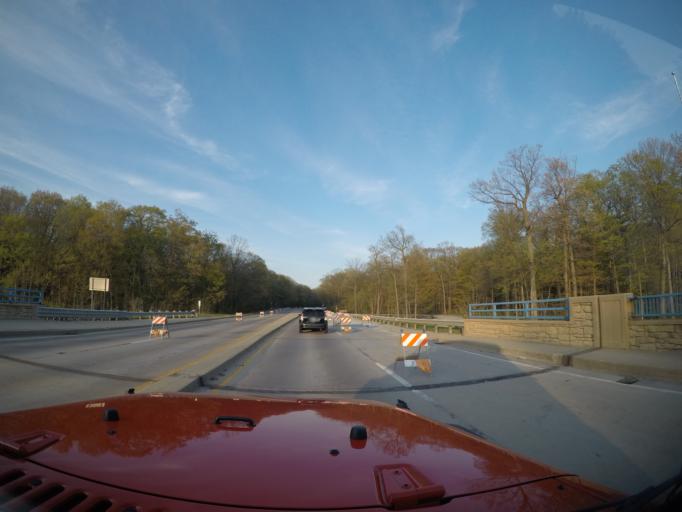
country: US
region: Illinois
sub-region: Cook County
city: Prospect Heights
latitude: 42.0874
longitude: -87.8870
